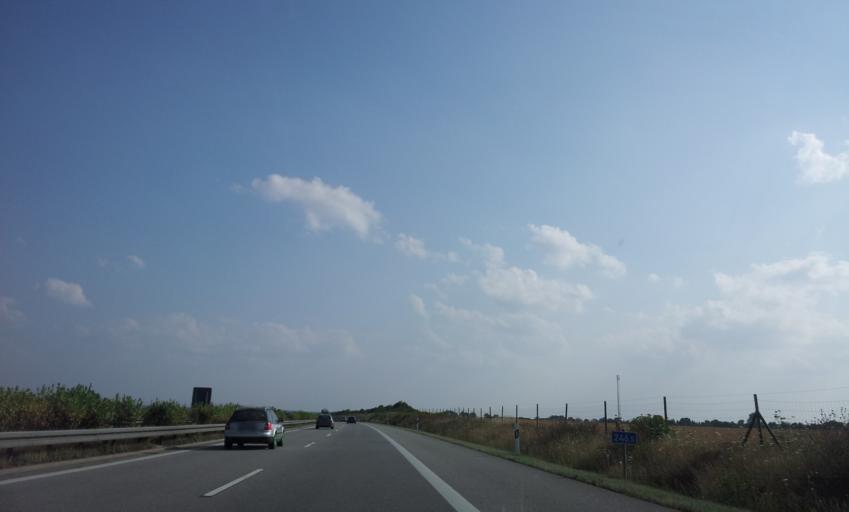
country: DE
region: Mecklenburg-Vorpommern
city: Kessin
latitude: 53.7045
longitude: 13.3269
